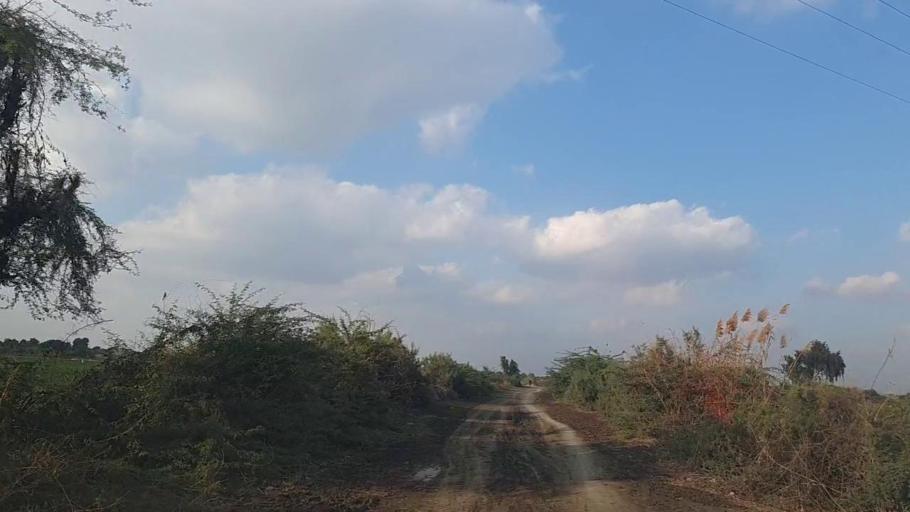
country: PK
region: Sindh
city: Tando Mittha Khan
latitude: 25.9390
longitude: 69.2510
